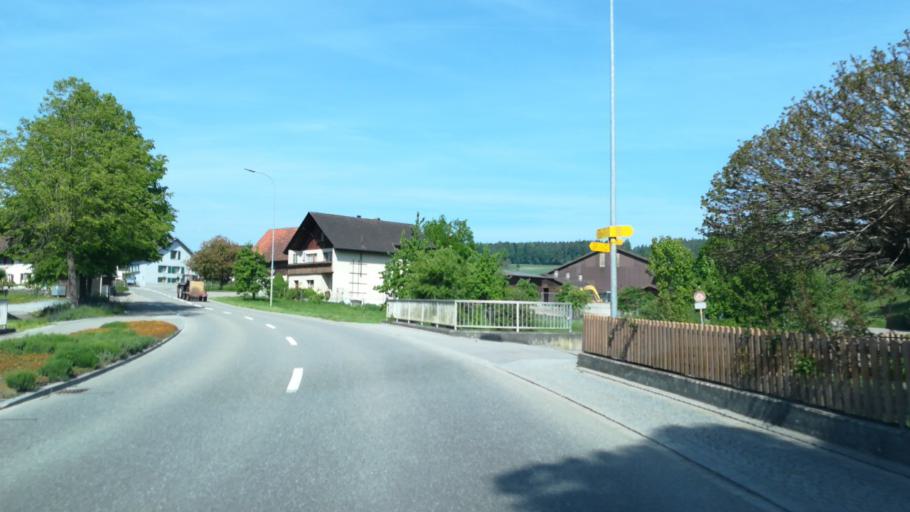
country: CH
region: Thurgau
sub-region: Frauenfeld District
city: Pfyn
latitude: 47.6011
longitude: 8.9503
